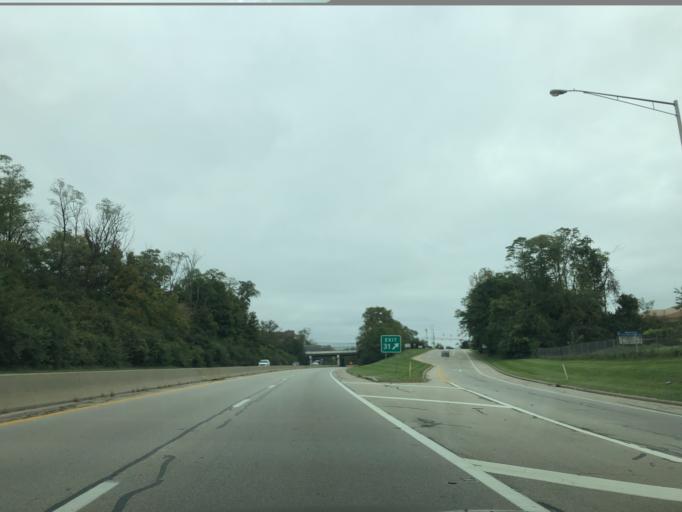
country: US
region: Ohio
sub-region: Hamilton County
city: Dillonvale
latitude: 39.2253
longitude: -84.3977
